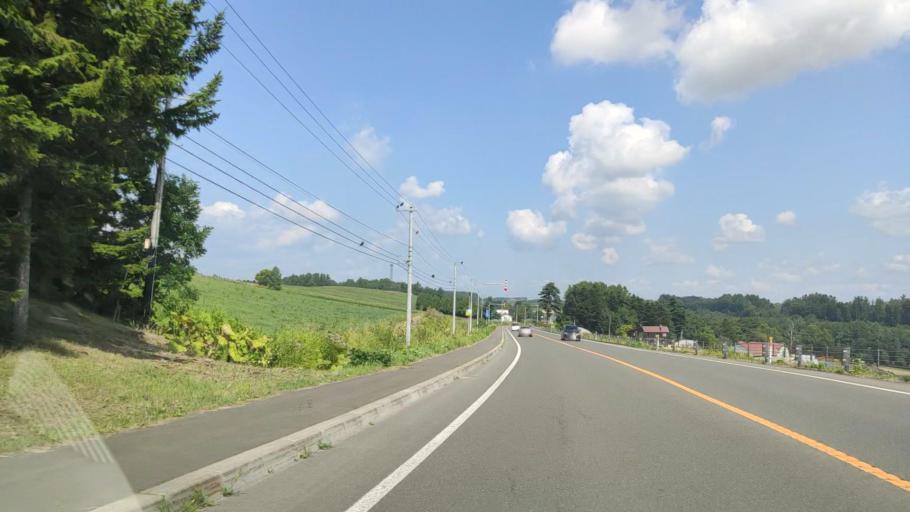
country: JP
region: Hokkaido
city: Shimo-furano
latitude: 43.5222
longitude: 142.4476
